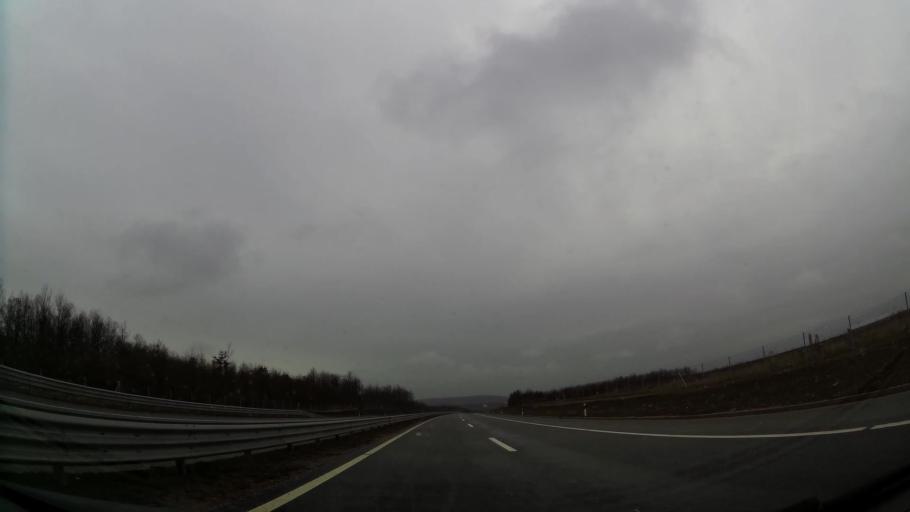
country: XK
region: Ferizaj
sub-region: Komuna e Ferizajt
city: Ferizaj
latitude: 42.3488
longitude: 21.2052
